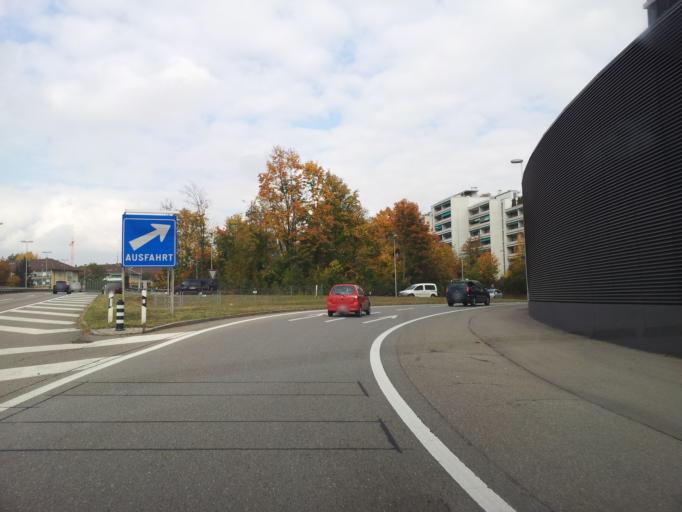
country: CH
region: Bern
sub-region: Bern-Mittelland District
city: Muri
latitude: 46.9436
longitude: 7.4728
